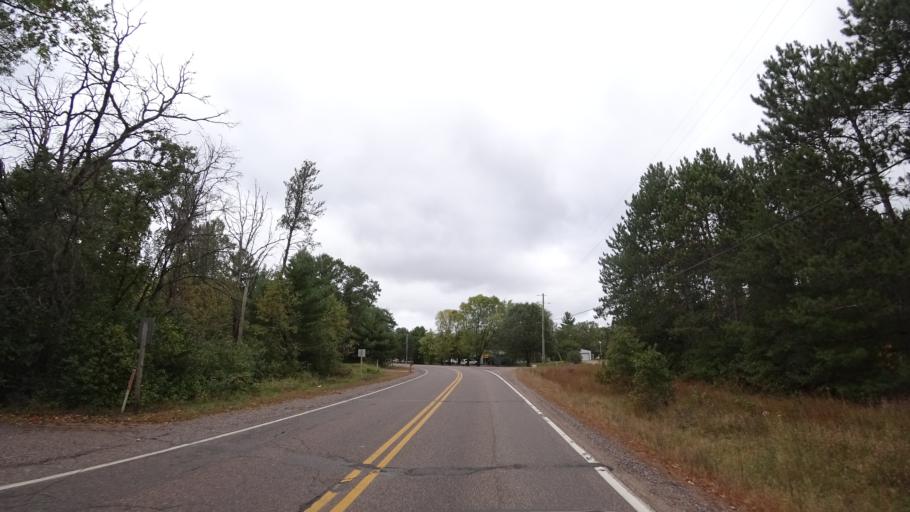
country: US
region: Wisconsin
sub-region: Chippewa County
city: Lake Wissota
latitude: 44.9475
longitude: -91.2628
